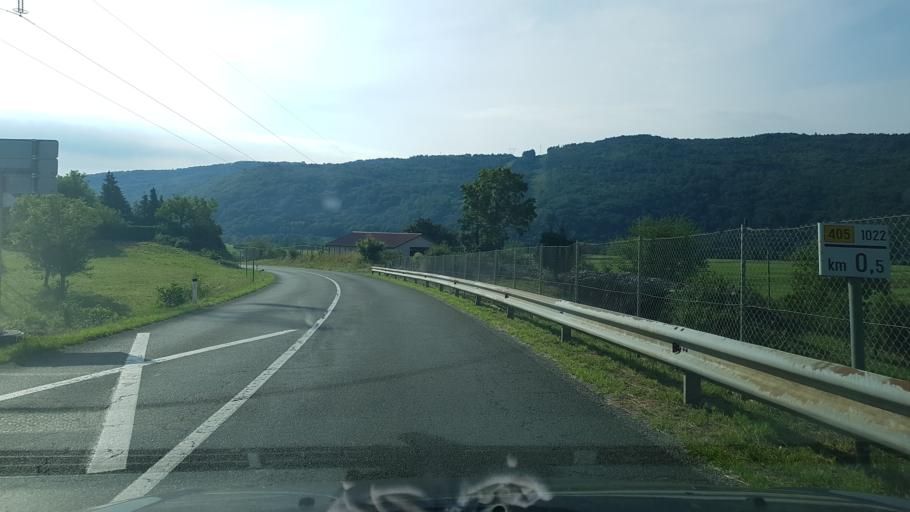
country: SI
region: Divaca
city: Divaca
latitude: 45.6563
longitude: 14.0312
